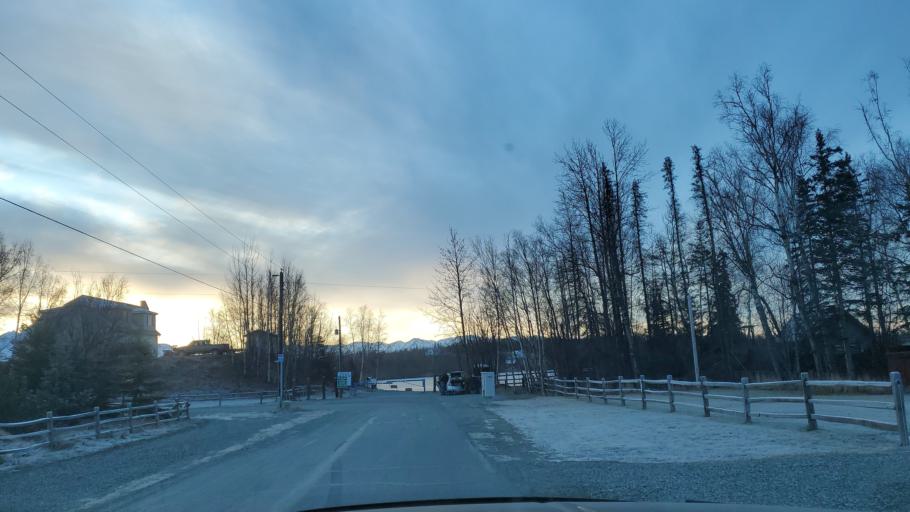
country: US
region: Alaska
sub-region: Matanuska-Susitna Borough
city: Lakes
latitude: 61.6010
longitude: -149.3164
